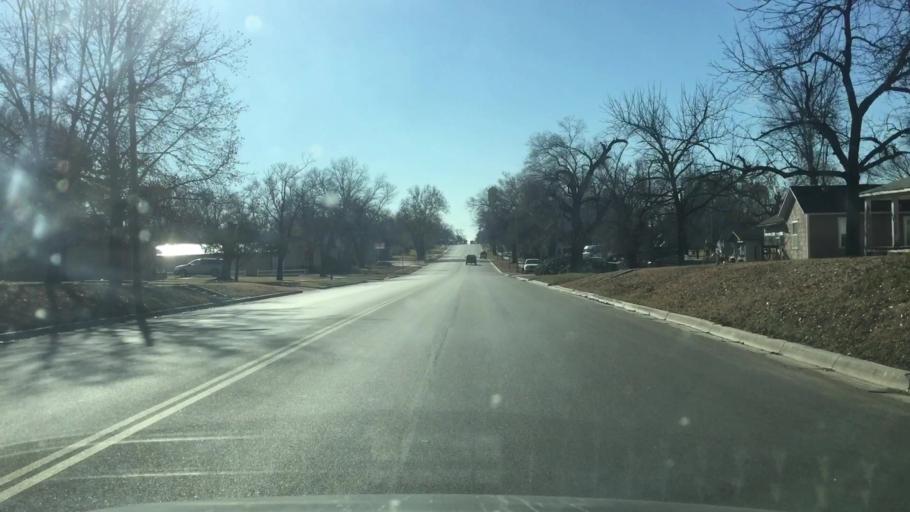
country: US
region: Kansas
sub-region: Allen County
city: Humboldt
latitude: 37.8167
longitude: -95.4356
